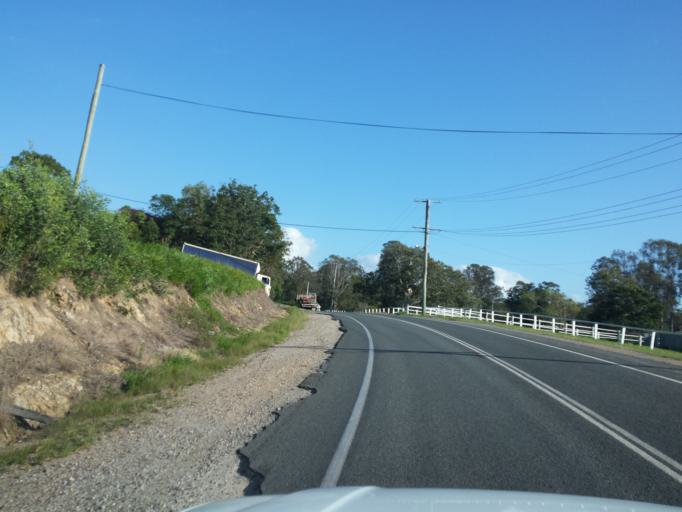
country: AU
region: Queensland
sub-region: Logan
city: Windaroo
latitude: -27.7680
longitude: 153.1912
